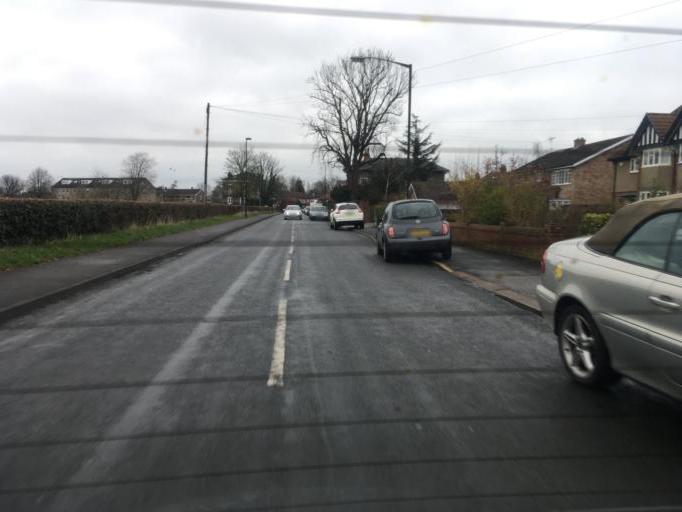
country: GB
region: England
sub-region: City of York
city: York
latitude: 53.9685
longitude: -1.0617
